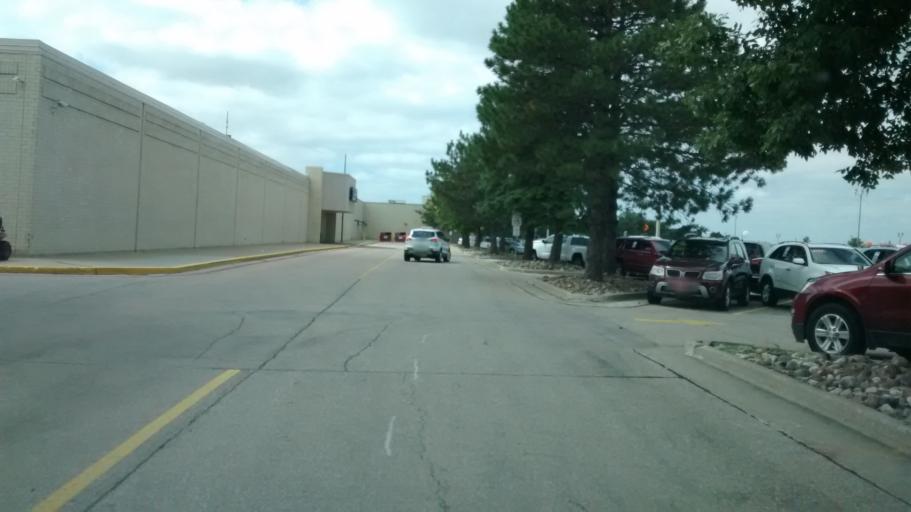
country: US
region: Iowa
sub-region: Woodbury County
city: Sergeant Bluff
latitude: 42.4463
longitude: -96.3495
